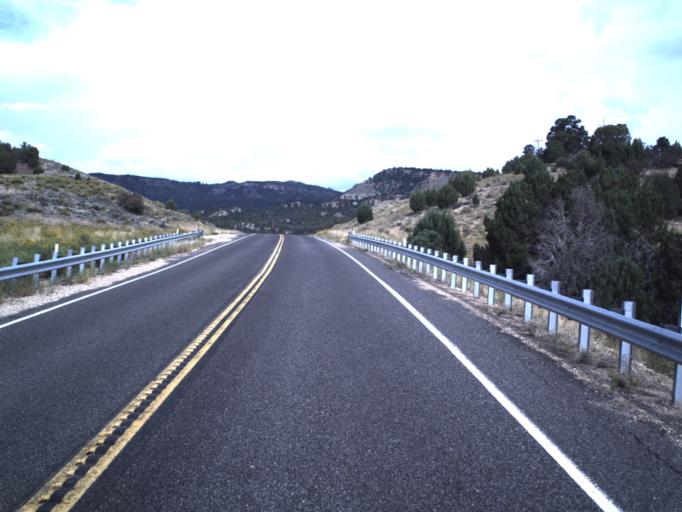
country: US
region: Utah
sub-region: Kane County
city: Kanab
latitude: 37.2595
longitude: -112.7677
